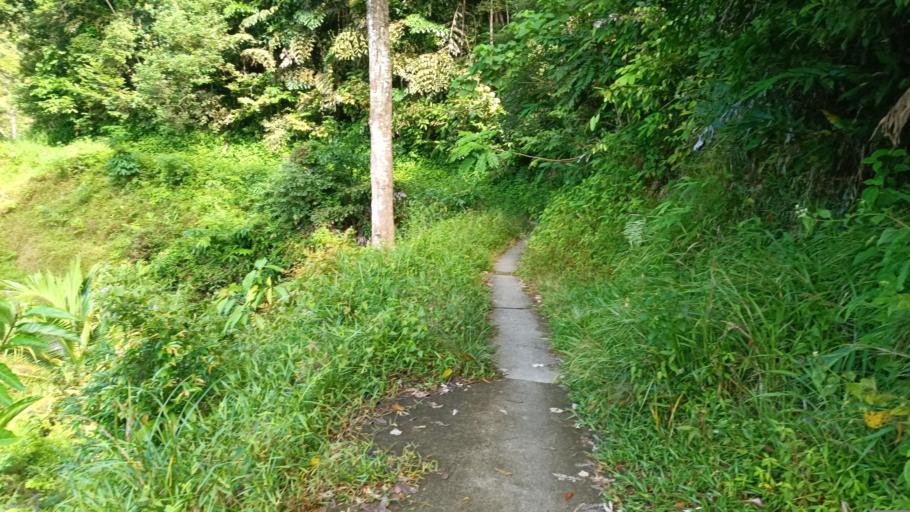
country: MY
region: Penang
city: Tanjung Tokong
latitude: 5.4189
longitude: 100.2806
